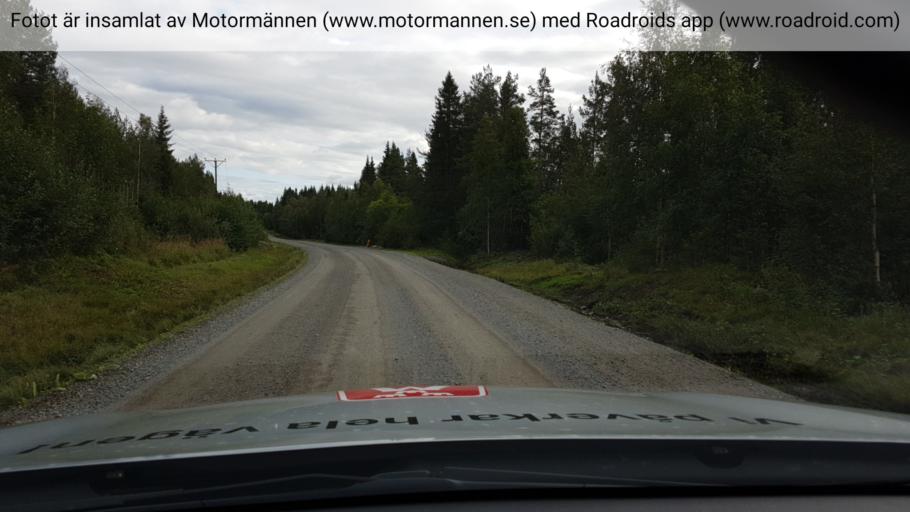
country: SE
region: Jaemtland
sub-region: Ragunda Kommun
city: Hammarstrand
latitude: 62.9417
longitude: 16.1123
